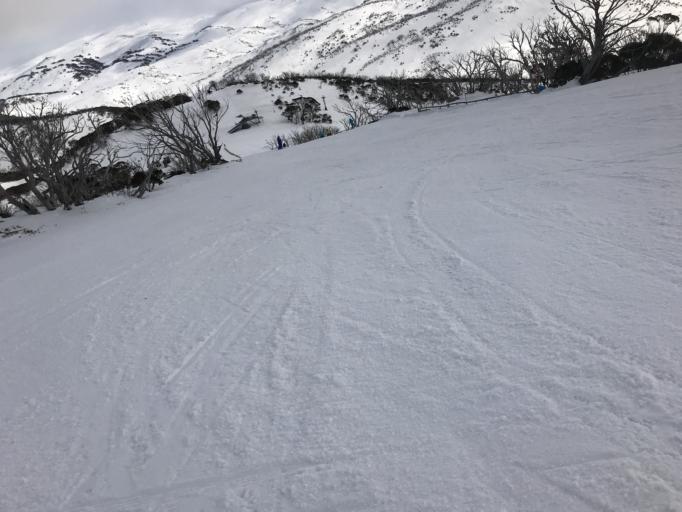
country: AU
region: New South Wales
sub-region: Snowy River
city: Jindabyne
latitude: -36.3815
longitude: 148.3830
